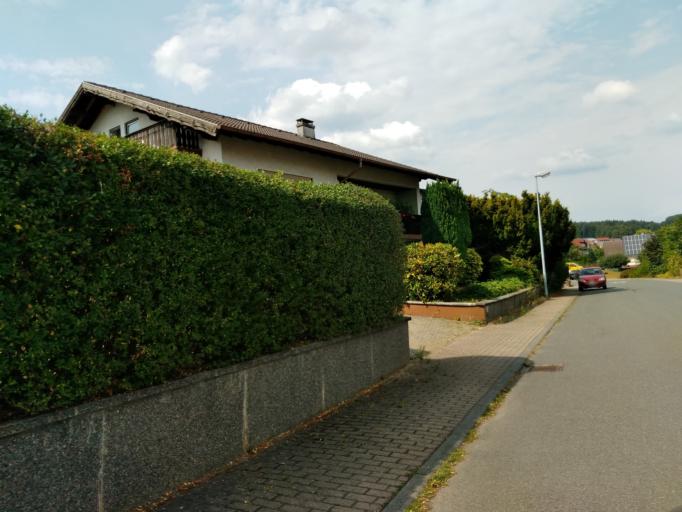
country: DE
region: Baden-Wuerttemberg
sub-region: Karlsruhe Region
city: Limbach
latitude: 49.4577
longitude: 9.2072
